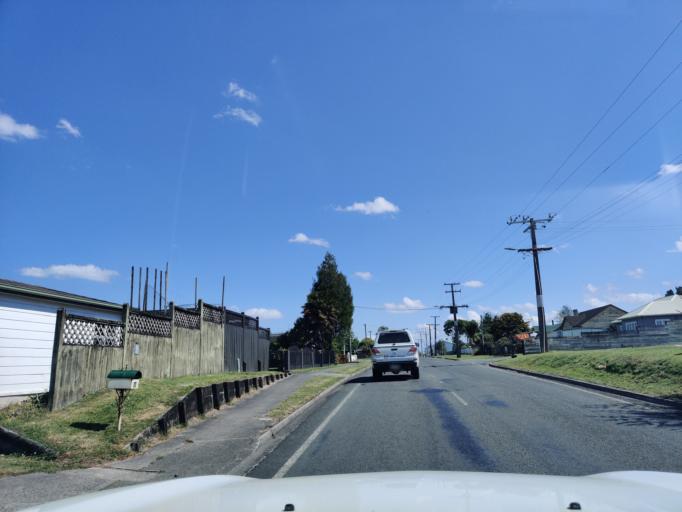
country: NZ
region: Waikato
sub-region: Waikato District
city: Ngaruawahia
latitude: -37.6612
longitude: 175.1434
